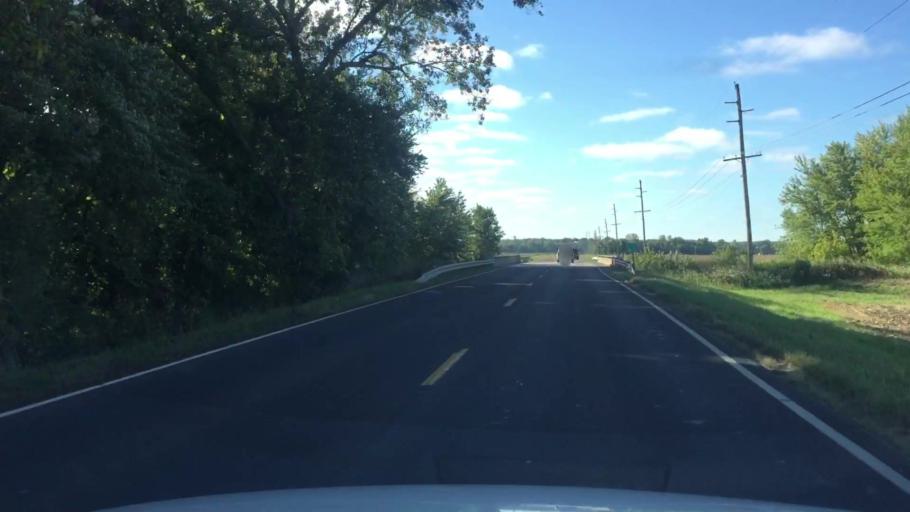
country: US
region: Missouri
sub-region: Howard County
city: New Franklin
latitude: 39.0071
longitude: -92.7382
